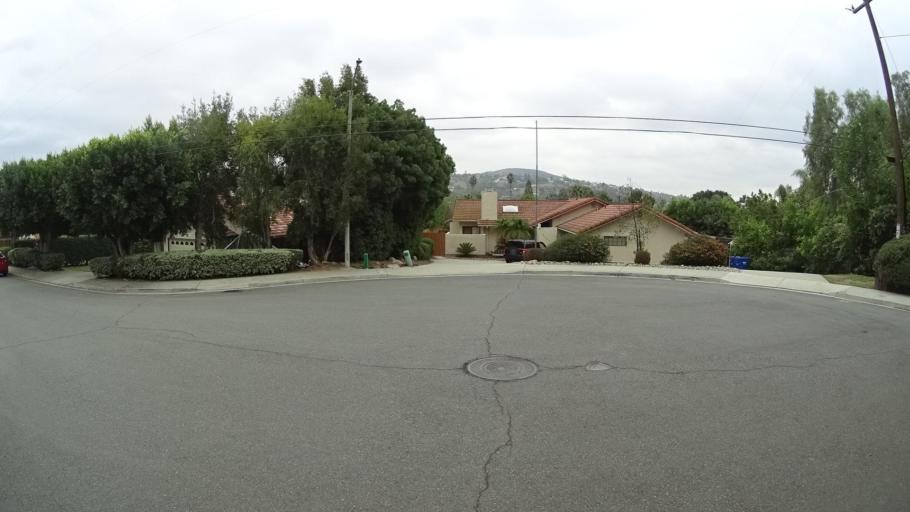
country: US
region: California
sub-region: San Diego County
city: Spring Valley
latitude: 32.7464
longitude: -116.9970
